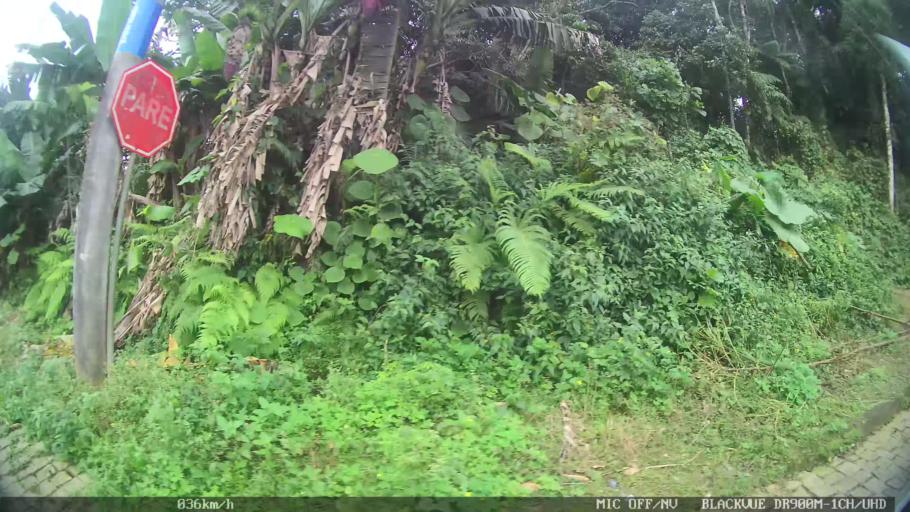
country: BR
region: Santa Catarina
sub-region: Joinville
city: Joinville
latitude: -26.2808
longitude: -48.8822
